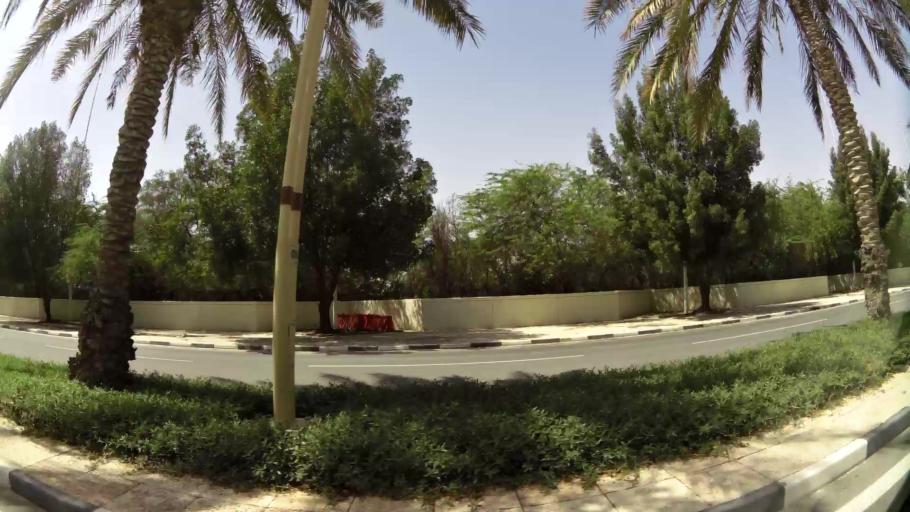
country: QA
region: Baladiyat ad Dawhah
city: Doha
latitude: 25.3675
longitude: 51.4951
